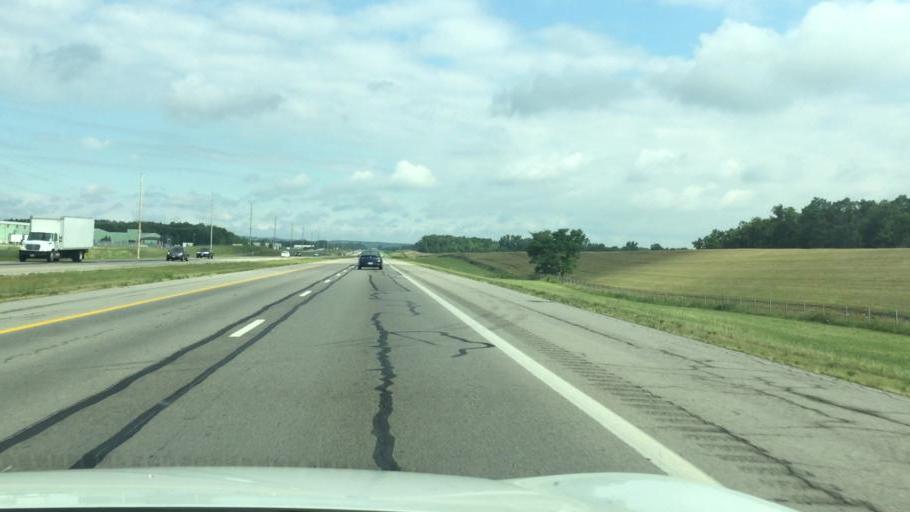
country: US
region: Ohio
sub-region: Champaign County
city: North Lewisburg
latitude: 40.2876
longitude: -83.5506
